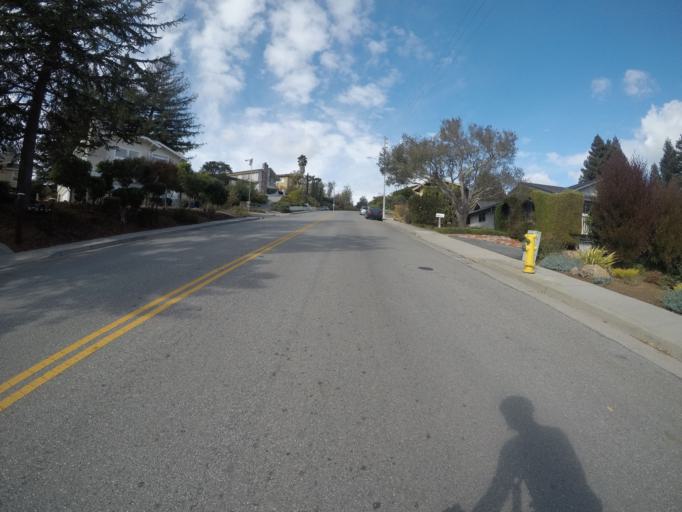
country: US
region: California
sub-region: Santa Cruz County
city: Pasatiempo
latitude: 36.9961
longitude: -122.0139
